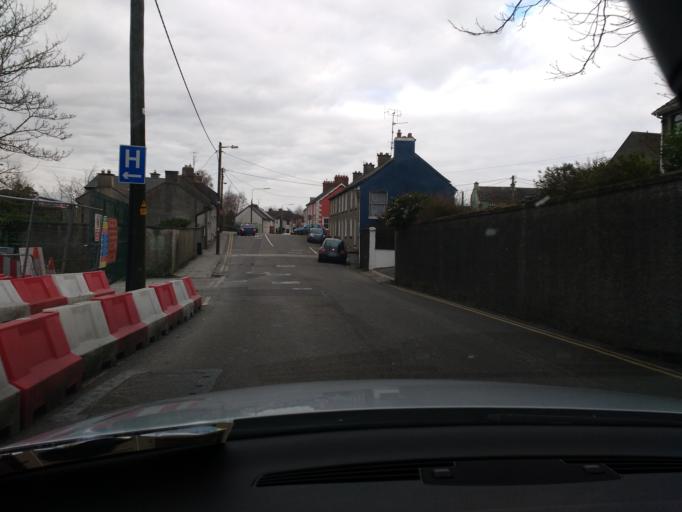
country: IE
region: Leinster
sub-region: Kilkenny
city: Kilkenny
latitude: 52.6577
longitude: -7.2523
